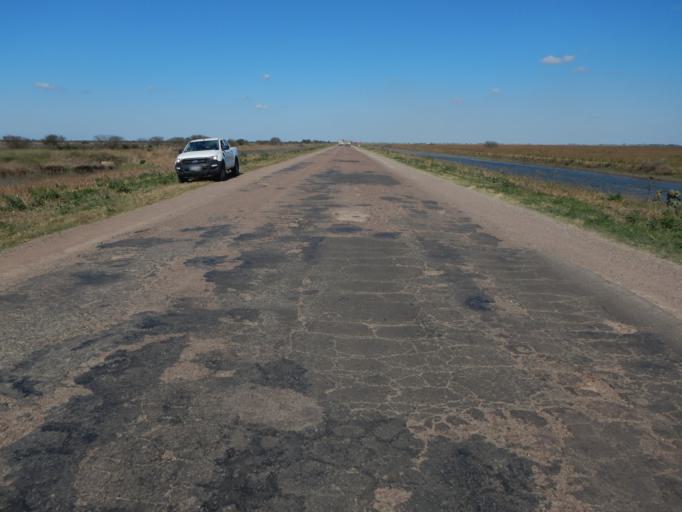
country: AR
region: Santa Fe
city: Tostado
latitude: -28.6845
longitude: -61.5331
